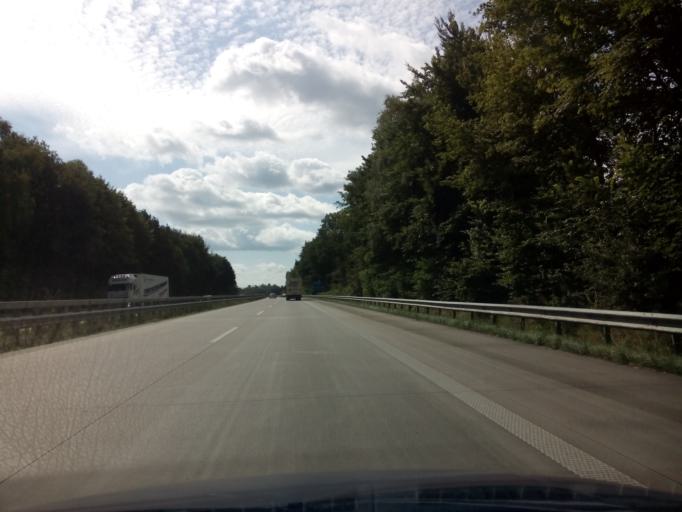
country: DE
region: Lower Saxony
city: Schwanewede
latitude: 53.2188
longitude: 8.6486
